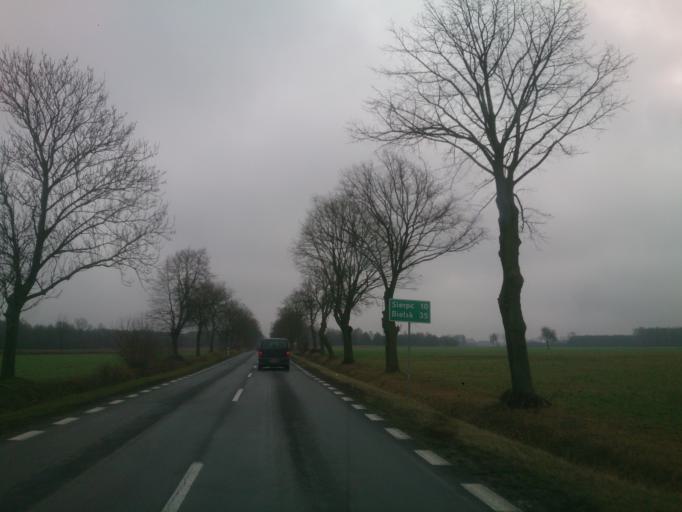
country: PL
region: Masovian Voivodeship
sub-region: Powiat sierpecki
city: Szczutowo
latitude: 52.9325
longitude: 19.5994
